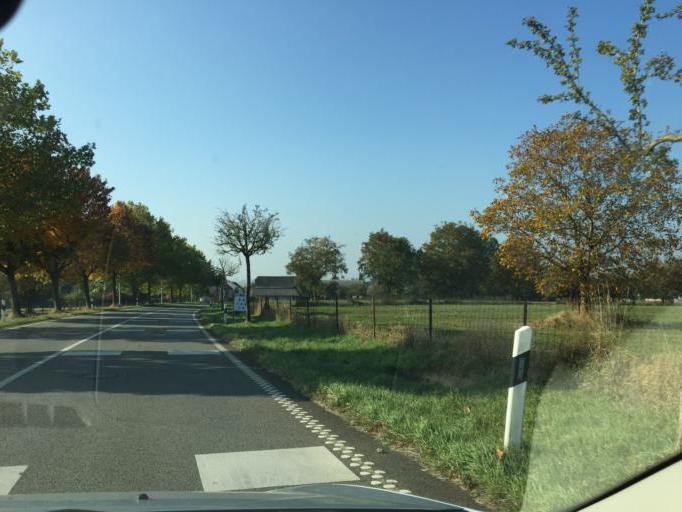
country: LU
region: Grevenmacher
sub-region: Canton de Remich
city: Dalheim
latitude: 49.5367
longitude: 6.2514
